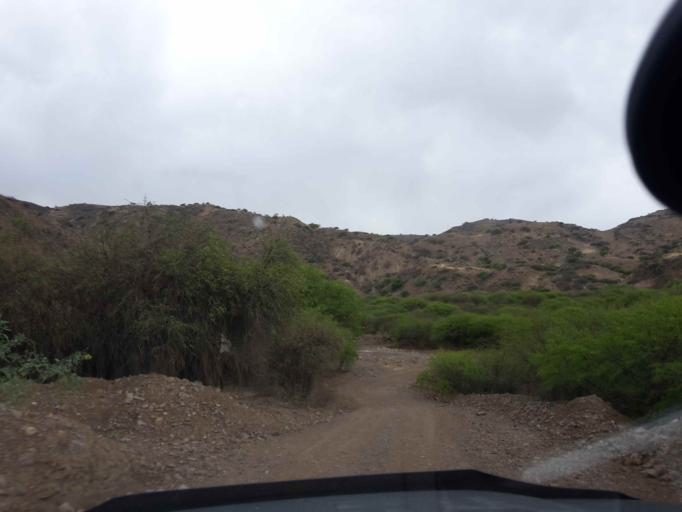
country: BO
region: Cochabamba
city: Sipe Sipe
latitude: -17.5292
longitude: -66.5197
